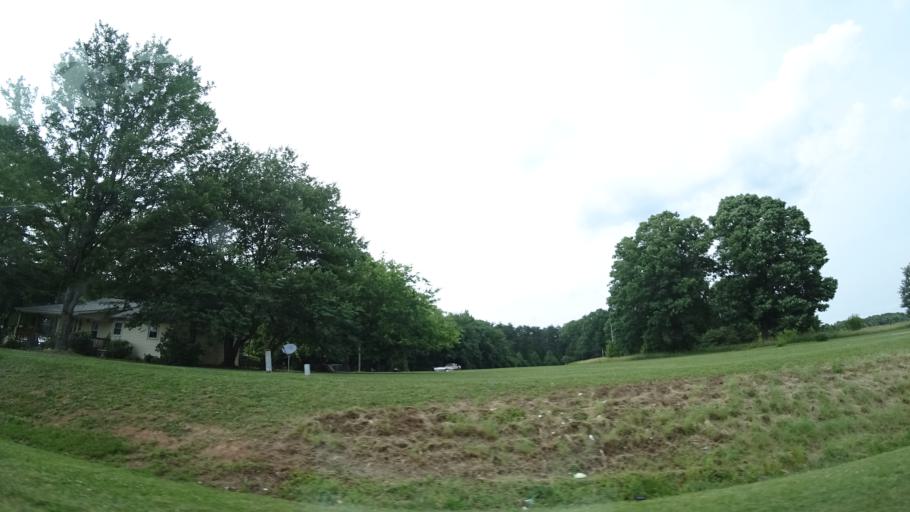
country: US
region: Virginia
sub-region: Spotsylvania County
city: Spotsylvania
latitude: 38.1478
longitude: -77.7105
